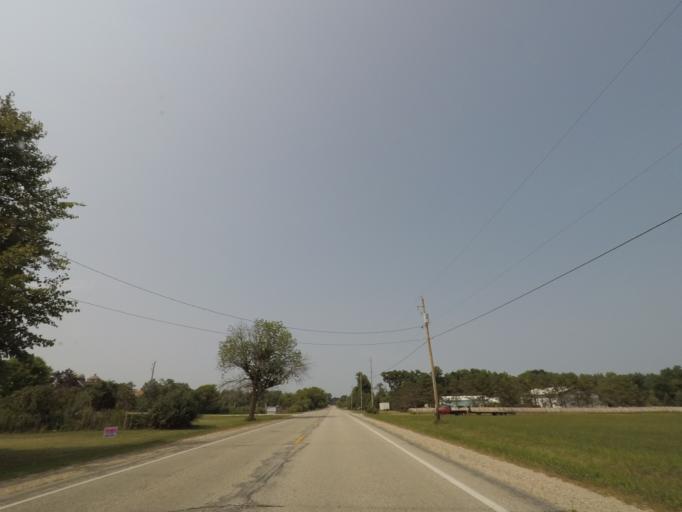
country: US
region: Wisconsin
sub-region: Waukesha County
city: Oconomowoc
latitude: 43.0607
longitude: -88.5083
